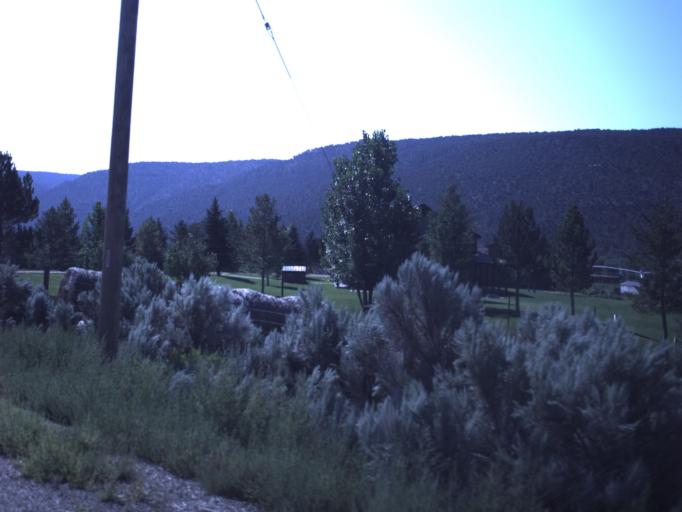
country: US
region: Utah
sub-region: Duchesne County
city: Duchesne
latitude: 40.3181
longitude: -110.6537
